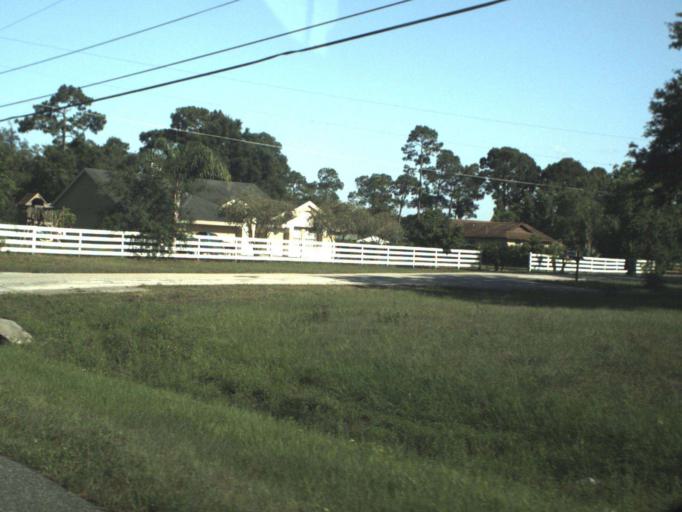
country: US
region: Florida
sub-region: Seminole County
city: Geneva
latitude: 28.7278
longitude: -81.1060
